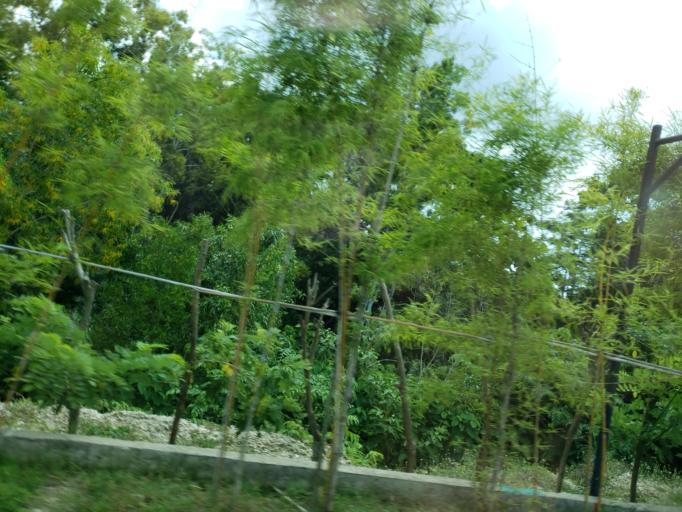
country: ID
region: Bali
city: Kangin
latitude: -8.8421
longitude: 115.1292
